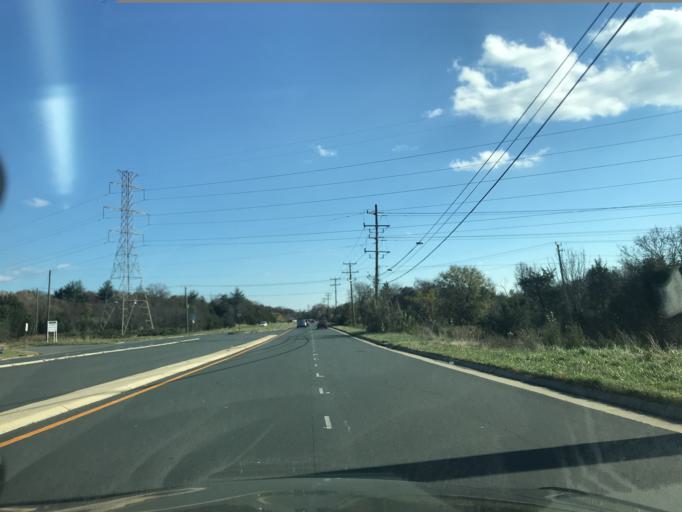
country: US
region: Virginia
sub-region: Fairfax County
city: Floris
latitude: 38.9467
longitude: -77.4270
